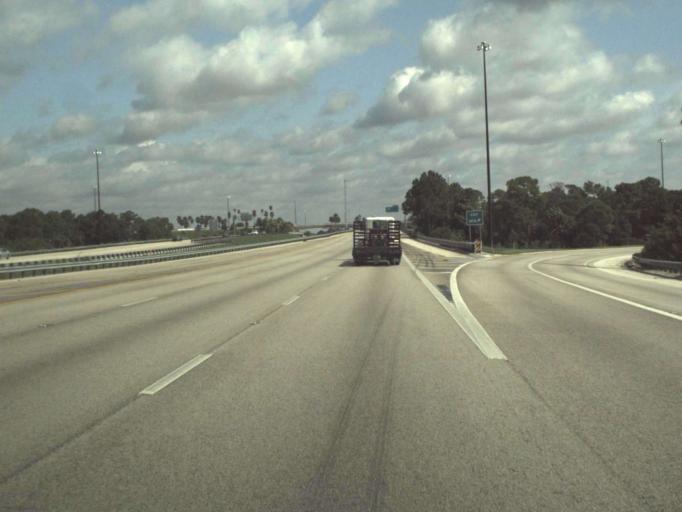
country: US
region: Florida
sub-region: Palm Beach County
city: Limestone Creek
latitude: 26.9308
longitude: -80.1488
